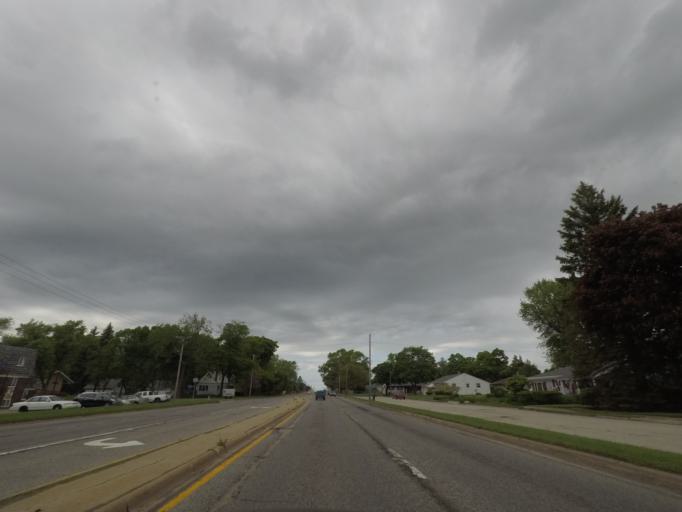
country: US
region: Illinois
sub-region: Winnebago County
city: Rockford
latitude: 42.2449
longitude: -89.0290
